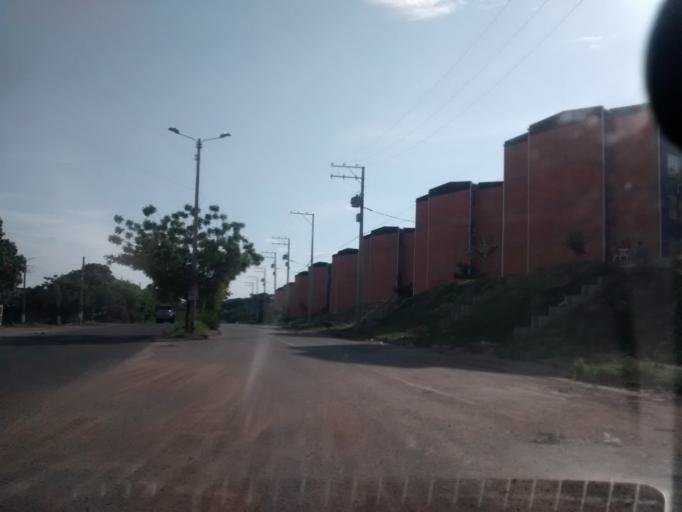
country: CO
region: Cundinamarca
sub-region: Girardot
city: Girardot City
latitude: 4.3227
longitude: -74.8051
